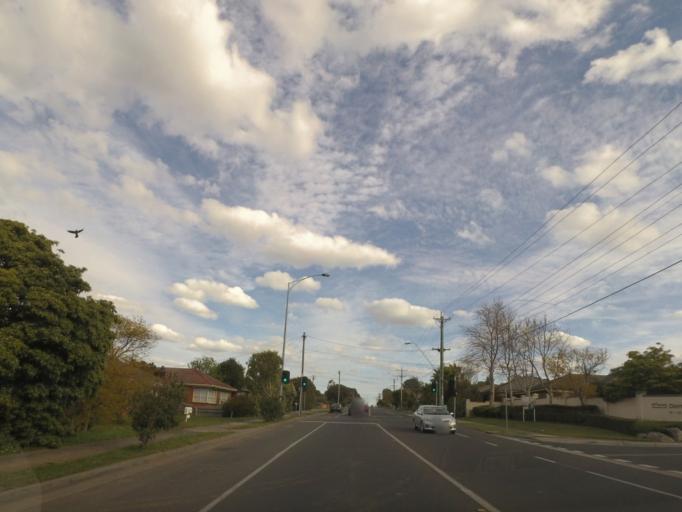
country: AU
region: Victoria
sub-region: Manningham
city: Doncaster East
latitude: -37.7832
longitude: 145.1444
